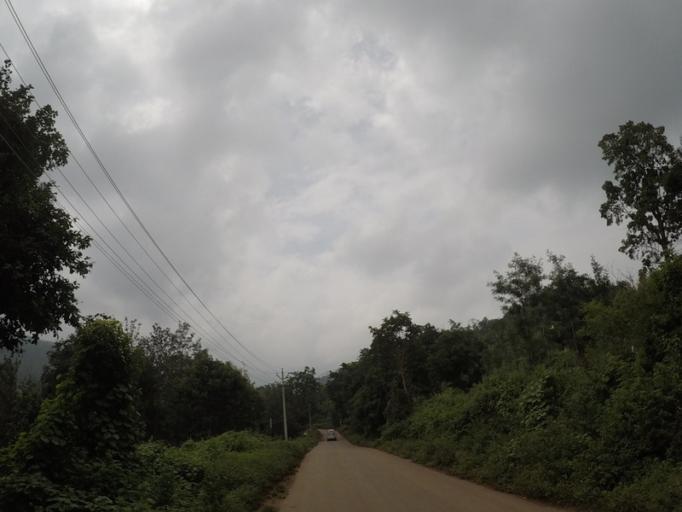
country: IN
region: Karnataka
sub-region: Chikmagalur
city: Birur
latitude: 13.5276
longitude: 75.8249
